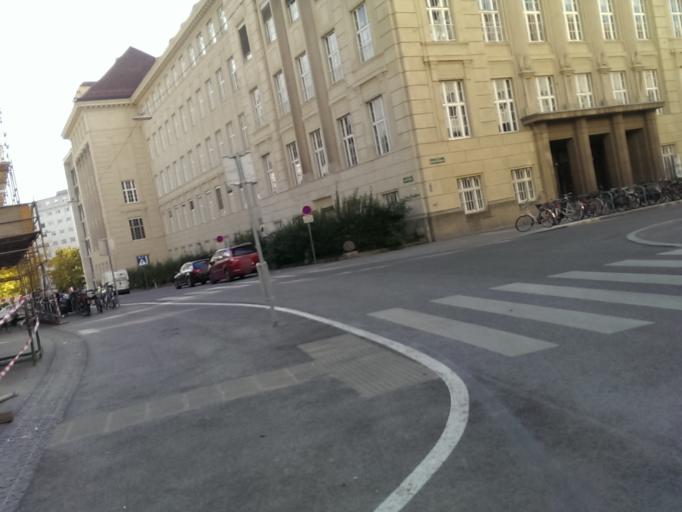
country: AT
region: Styria
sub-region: Graz Stadt
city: Graz
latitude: 47.0652
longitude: 15.4518
